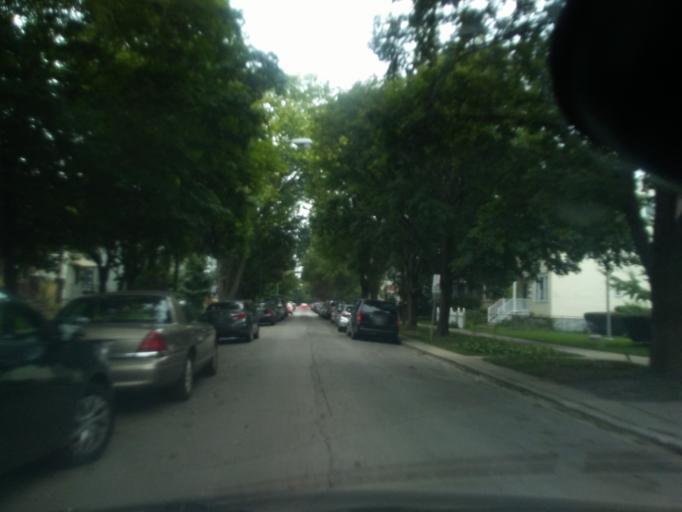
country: US
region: Illinois
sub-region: Cook County
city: Lincolnwood
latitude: 41.9688
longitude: -87.7549
